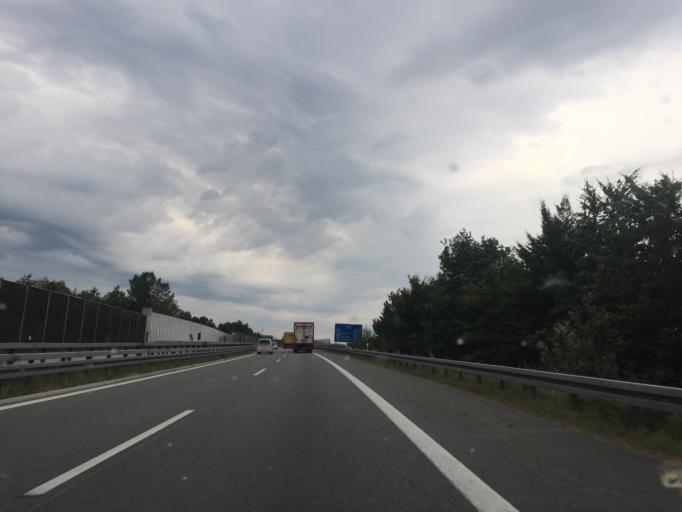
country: DE
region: Bavaria
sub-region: Upper Palatinate
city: Schirmitz
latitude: 49.6546
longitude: 12.1469
